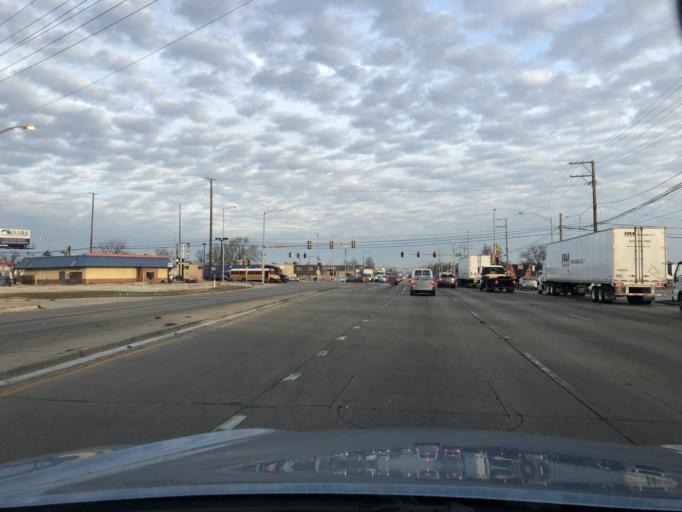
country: US
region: Illinois
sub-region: Cook County
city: Elk Grove Village
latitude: 42.0072
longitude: -87.9402
